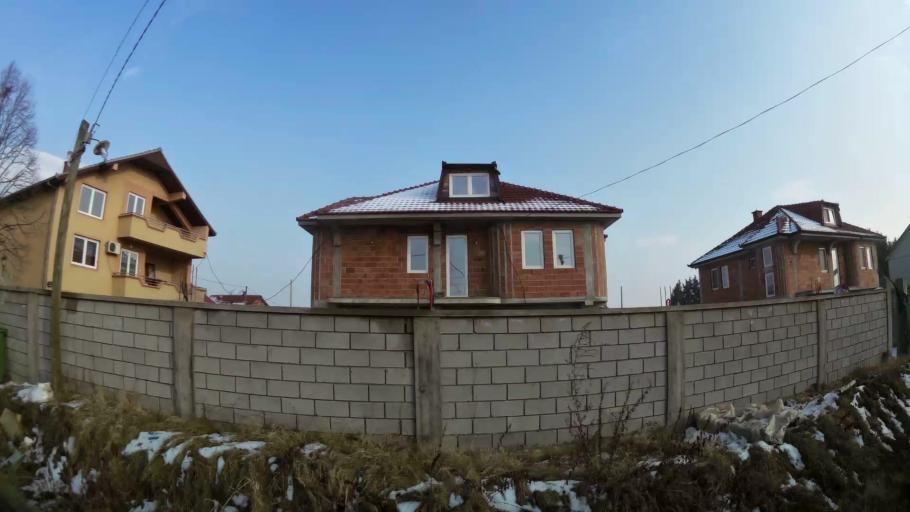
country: MK
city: Creshevo
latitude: 42.0219
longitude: 21.5095
